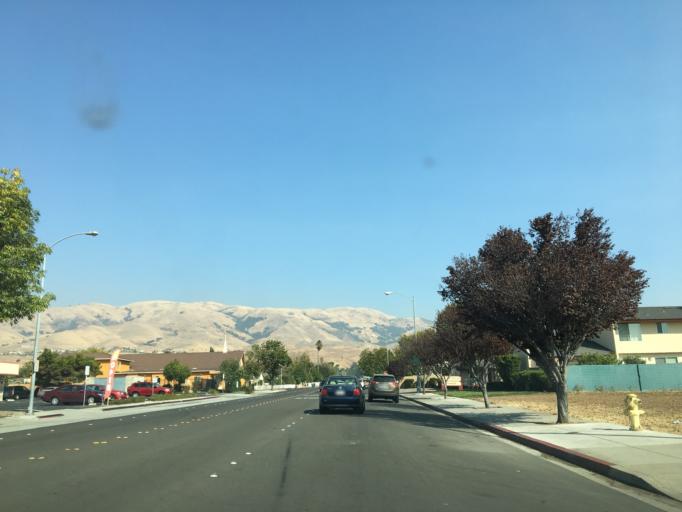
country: US
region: California
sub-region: Santa Clara County
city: Milpitas
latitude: 37.4579
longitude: -121.9101
